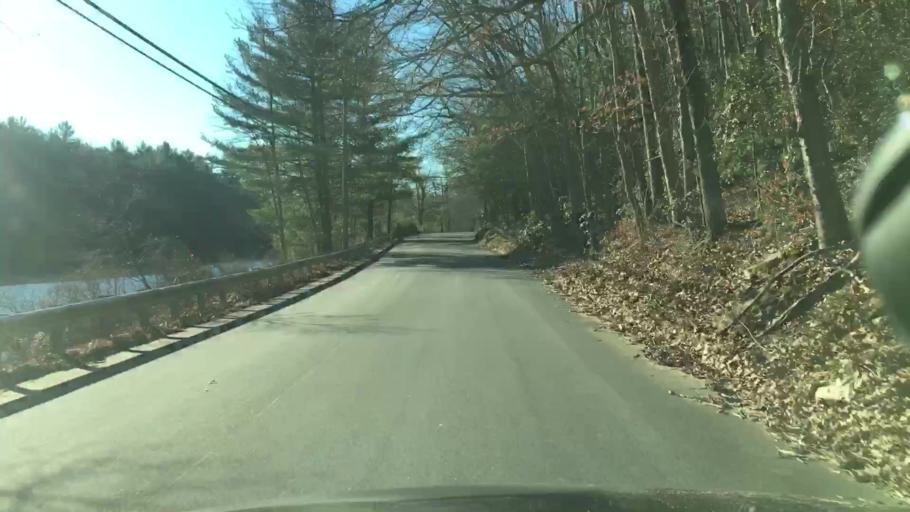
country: US
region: Connecticut
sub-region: Tolland County
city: Stafford
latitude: 41.9707
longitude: -72.2978
